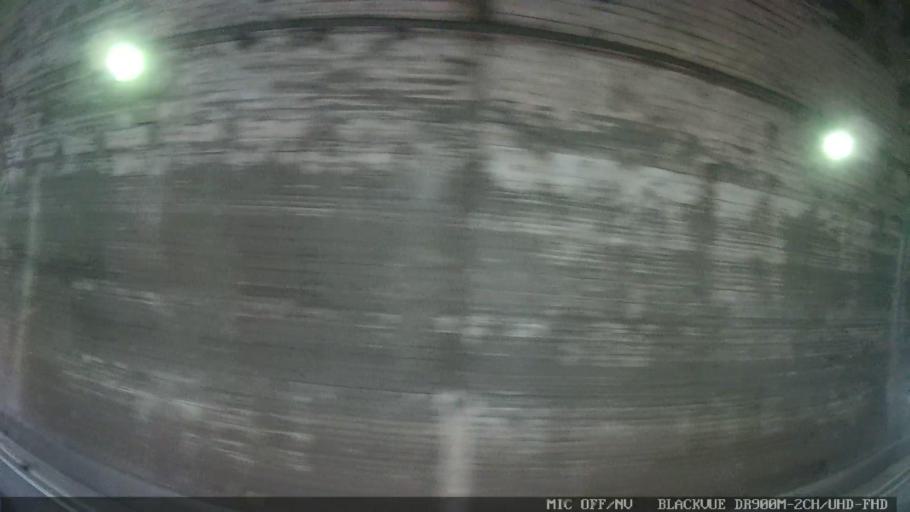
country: BR
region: Sao Paulo
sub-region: Cubatao
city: Cubatao
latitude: -23.8914
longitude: -46.4848
